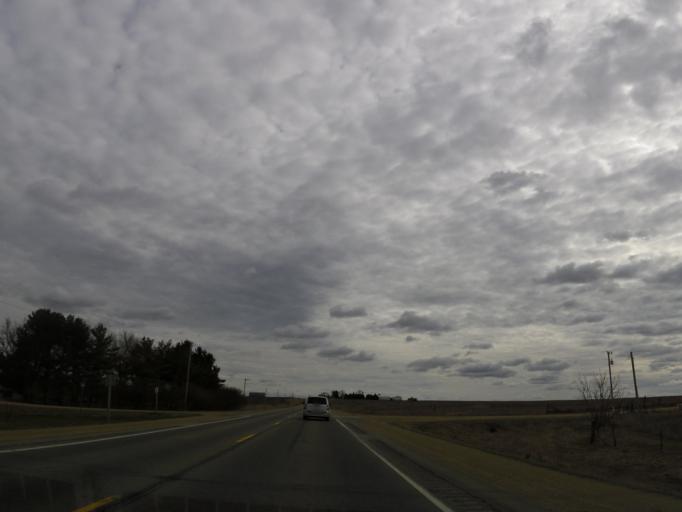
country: US
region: Iowa
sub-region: Chickasaw County
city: New Hampton
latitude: 43.1698
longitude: -92.2988
